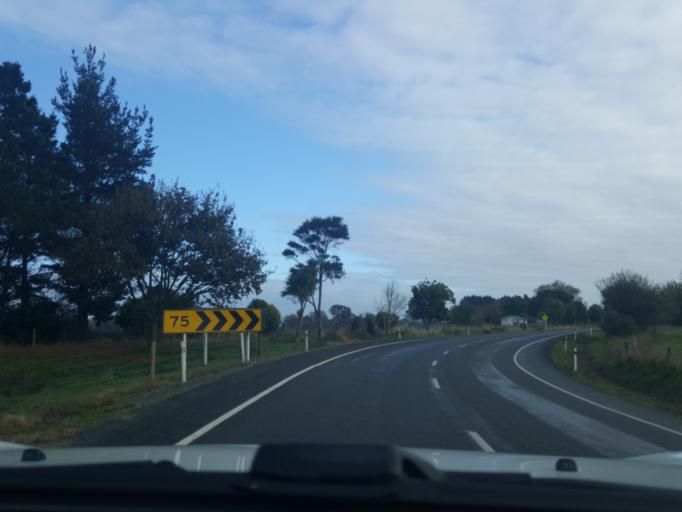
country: NZ
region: Waikato
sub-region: Hauraki District
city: Paeroa
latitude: -37.5049
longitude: 175.6883
